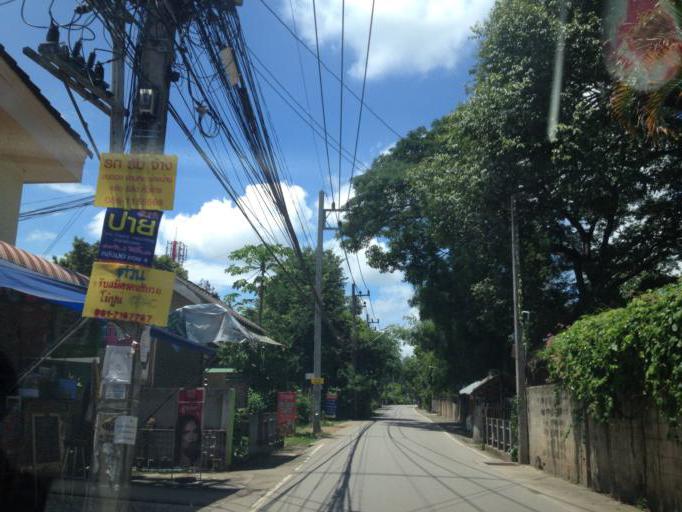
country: TH
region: Chiang Mai
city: Chiang Mai
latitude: 18.7823
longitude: 98.9540
